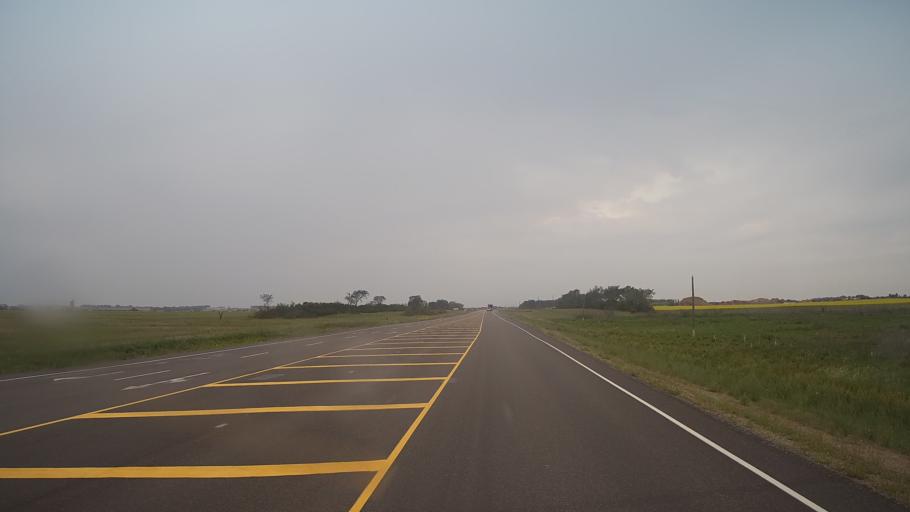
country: CA
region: Saskatchewan
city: Dalmeny
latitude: 52.1293
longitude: -106.8613
